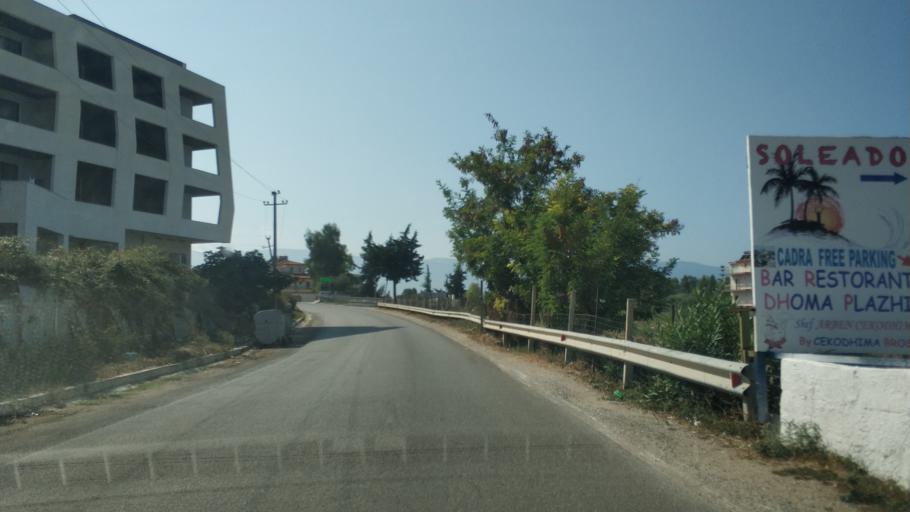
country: AL
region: Vlore
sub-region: Rrethi i Vlores
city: Orikum
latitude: 40.3784
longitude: 19.4812
